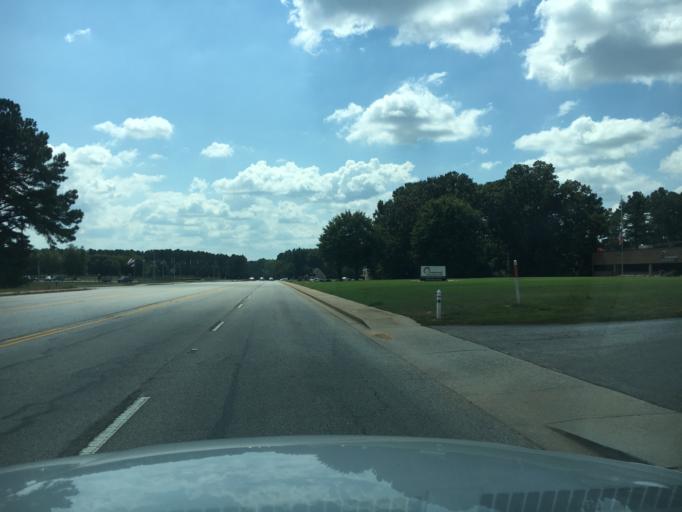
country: US
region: South Carolina
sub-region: Greenwood County
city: Greenwood
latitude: 34.2191
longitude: -82.2032
